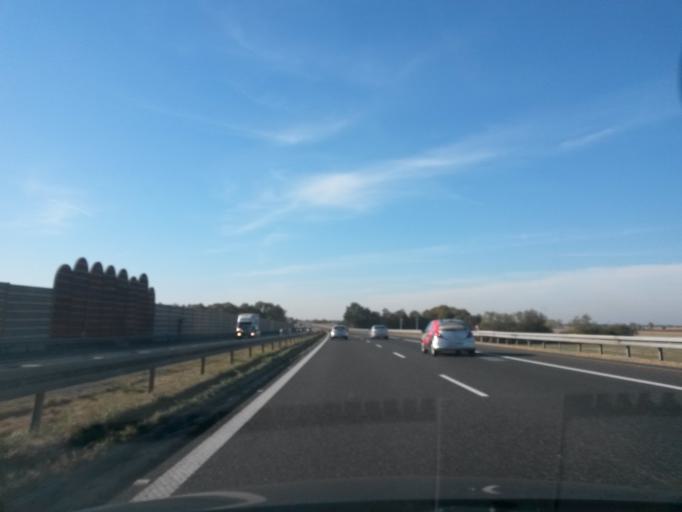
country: PL
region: Lower Silesian Voivodeship
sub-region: Powiat olawski
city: Wierzbno
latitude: 50.9349
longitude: 17.1119
